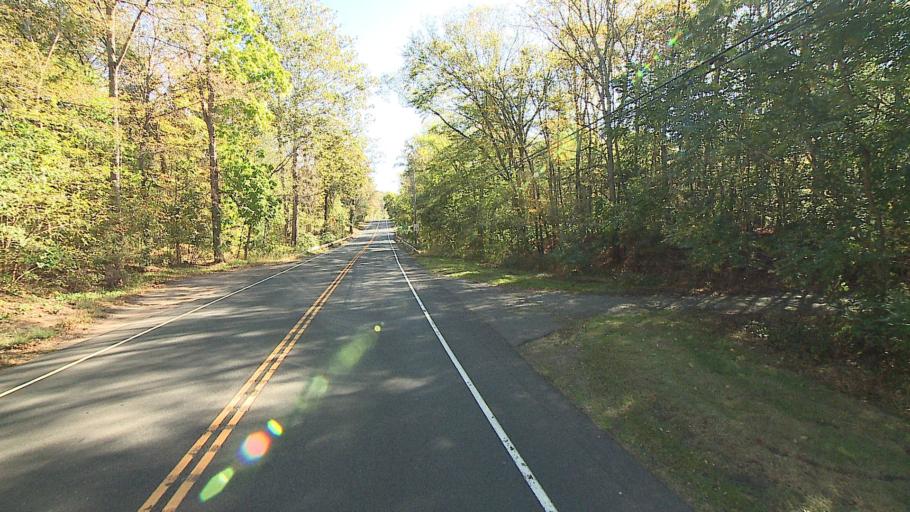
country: US
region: Connecticut
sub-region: Middlesex County
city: East Hampton
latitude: 41.5623
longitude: -72.5604
